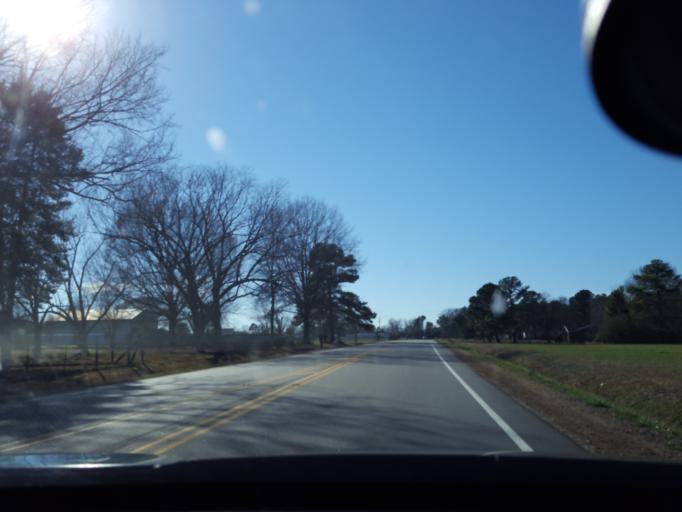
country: US
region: North Carolina
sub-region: Halifax County
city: South Rosemary
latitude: 36.4454
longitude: -77.7512
